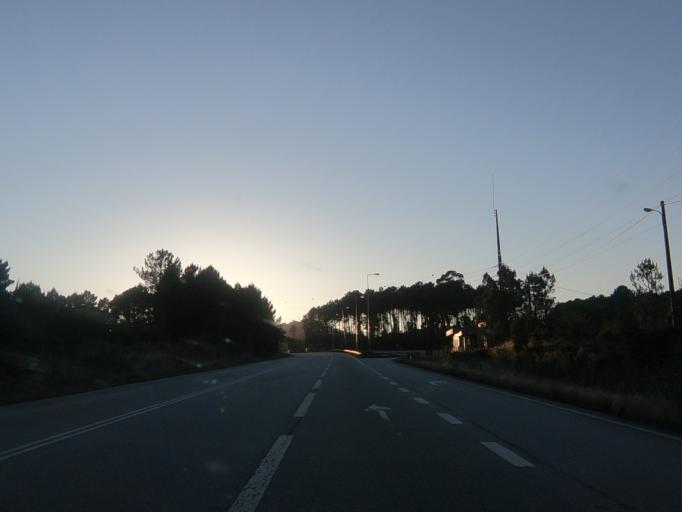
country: PT
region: Viseu
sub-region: Viseu
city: Abraveses
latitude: 40.6894
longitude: -7.9032
